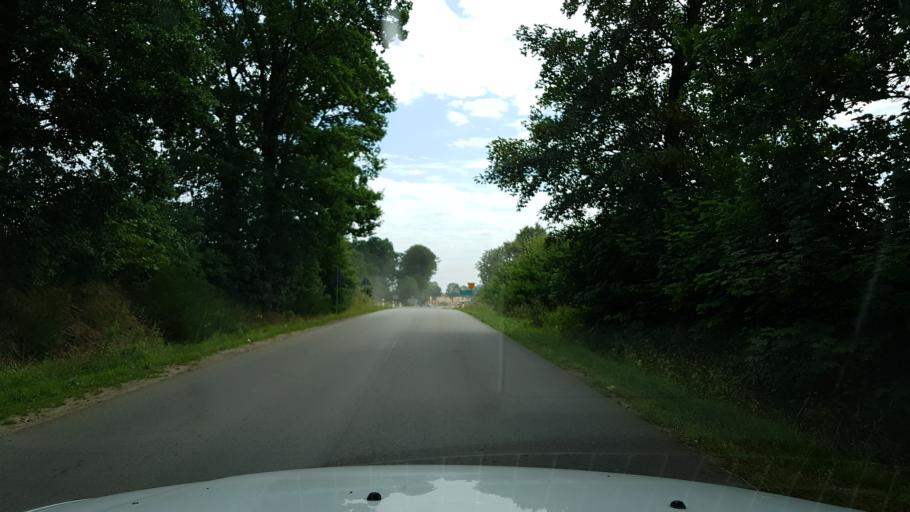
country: PL
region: West Pomeranian Voivodeship
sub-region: Koszalin
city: Koszalin
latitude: 54.1556
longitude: 16.0769
